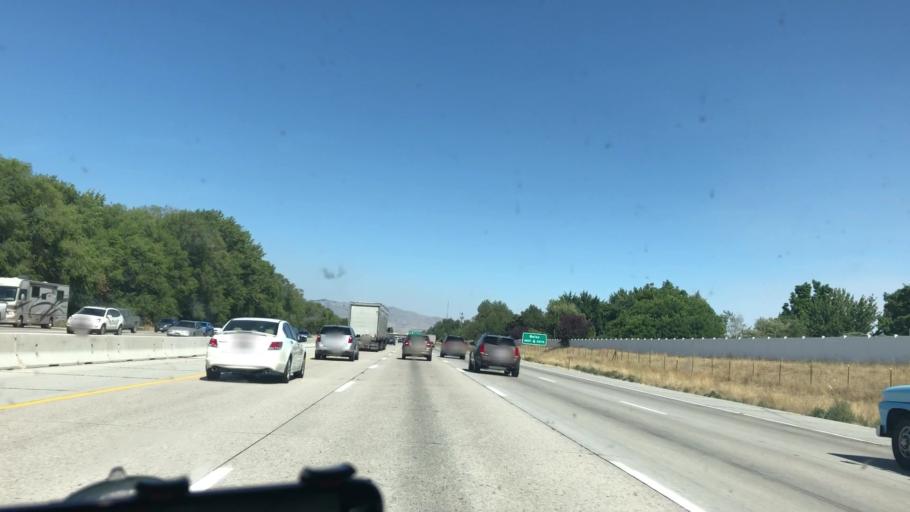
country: US
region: Idaho
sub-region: Ada County
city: Meridian
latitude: 43.5972
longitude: -116.3252
